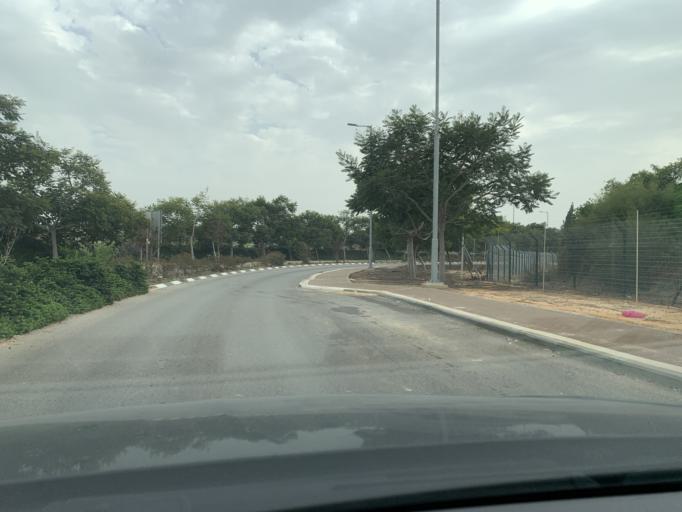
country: IL
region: Central District
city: Tirah
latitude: 32.2224
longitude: 34.9386
